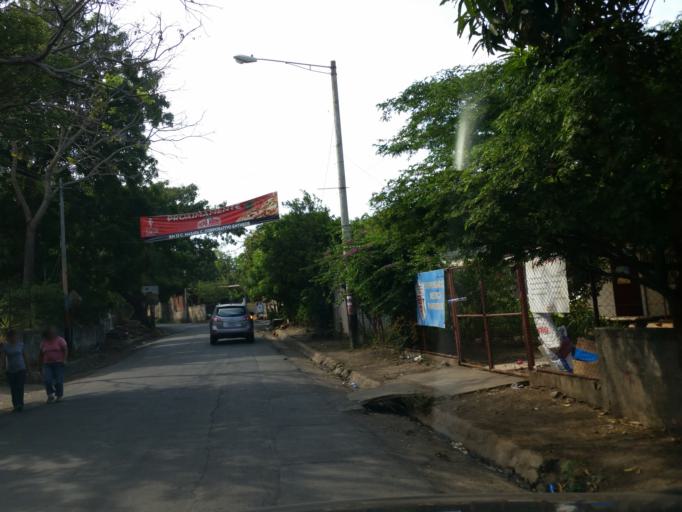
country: NI
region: Masaya
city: Ticuantepe
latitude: 12.0752
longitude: -86.2157
